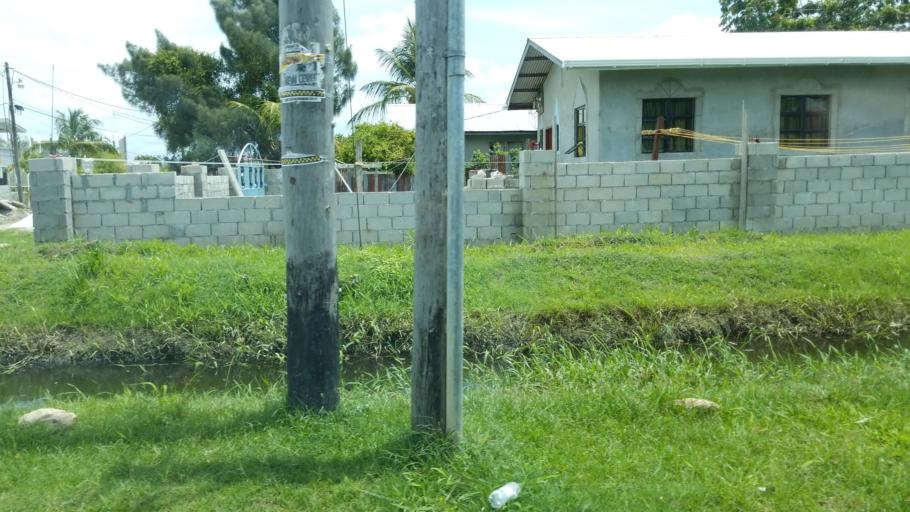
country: GY
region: Demerara-Mahaica
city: Georgetown
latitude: 6.7969
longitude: -58.1191
